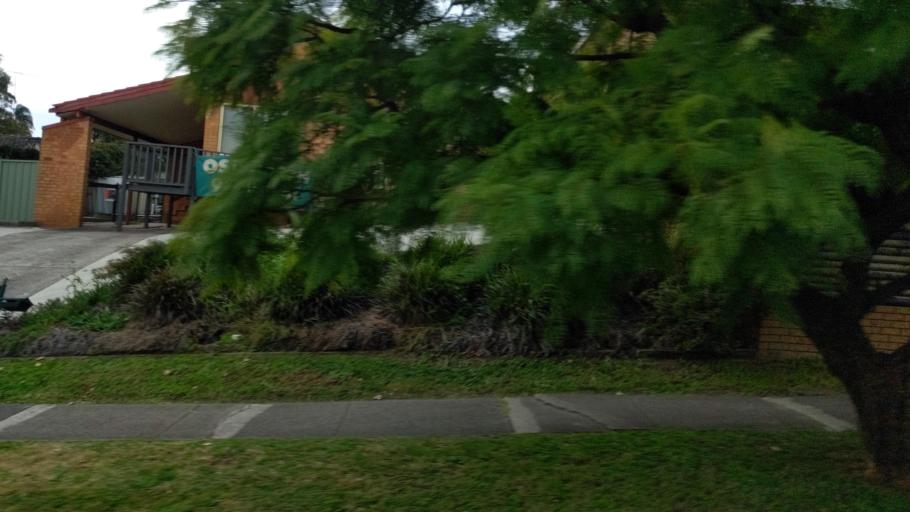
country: AU
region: New South Wales
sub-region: Blacktown
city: Blacktown
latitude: -33.7454
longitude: 150.9292
